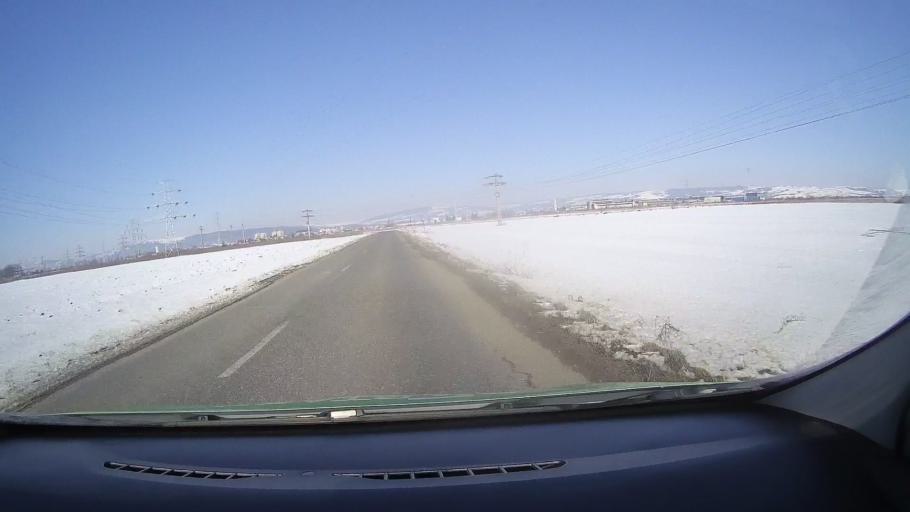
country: RO
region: Brasov
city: Fogarasch
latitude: 45.8162
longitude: 24.9874
